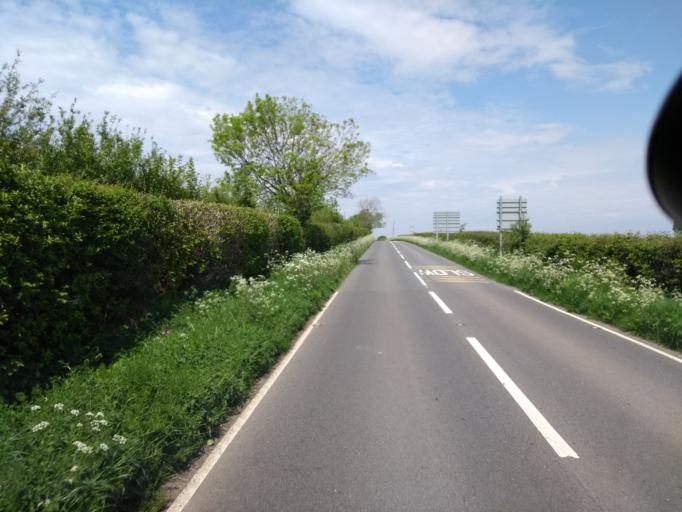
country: GB
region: England
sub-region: Somerset
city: Chard
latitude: 50.9049
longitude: -3.0026
